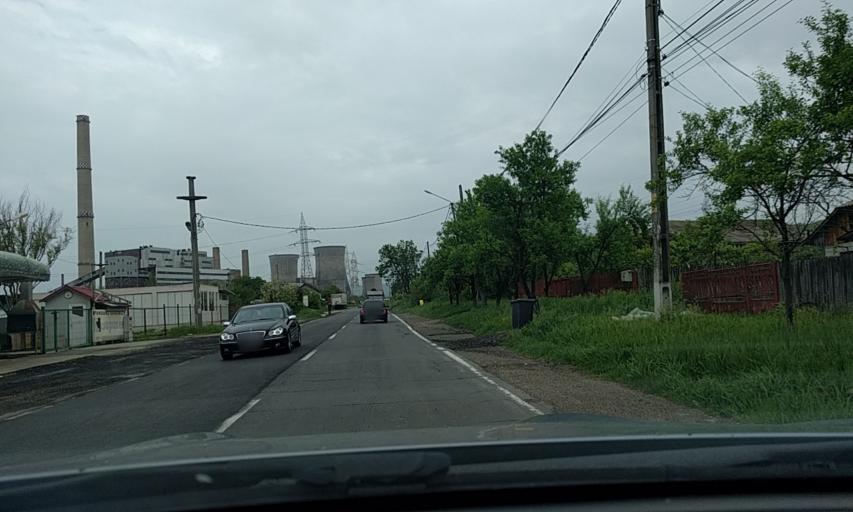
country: RO
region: Dambovita
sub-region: Comuna Doicesti
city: Doicesti
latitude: 44.9966
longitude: 25.4034
